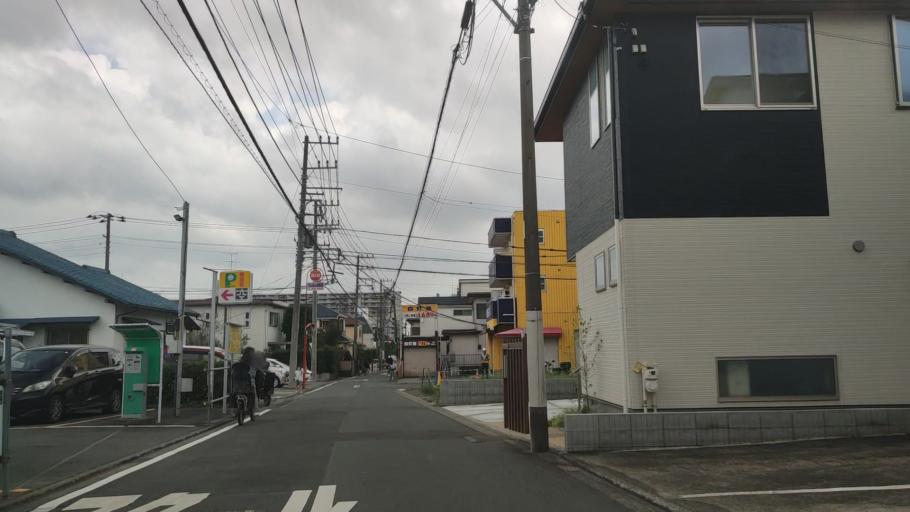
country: JP
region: Kanagawa
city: Minami-rinkan
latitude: 35.5106
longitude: 139.4480
